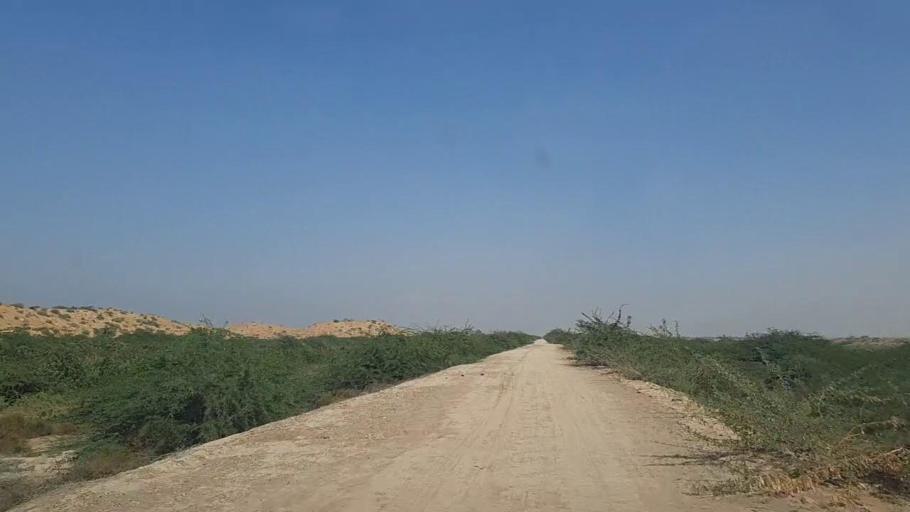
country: PK
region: Sindh
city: Daro Mehar
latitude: 24.8666
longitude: 68.0440
